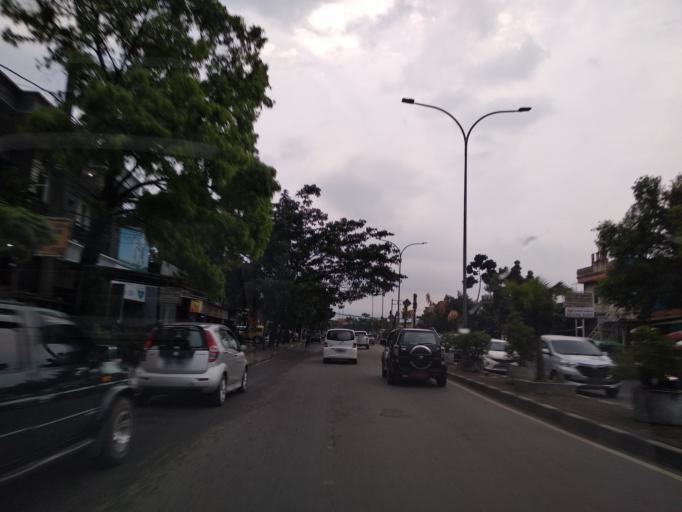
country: ID
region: West Java
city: Bandung
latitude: -6.9557
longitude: 107.6392
